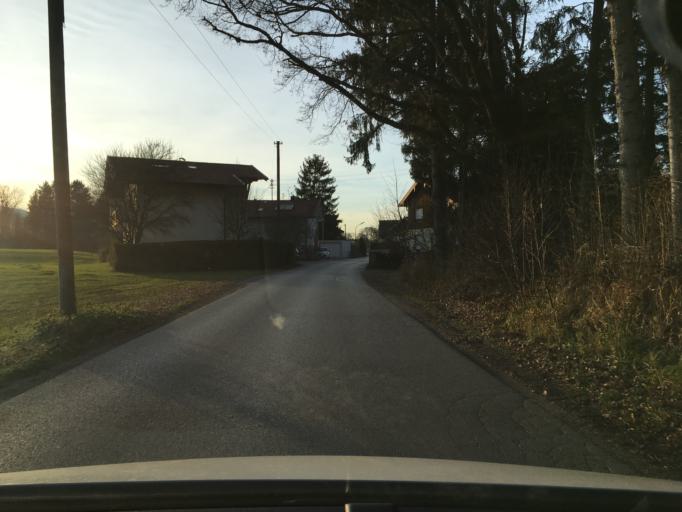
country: DE
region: Bavaria
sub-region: Upper Bavaria
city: Raubling
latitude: 47.7991
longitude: 12.1088
